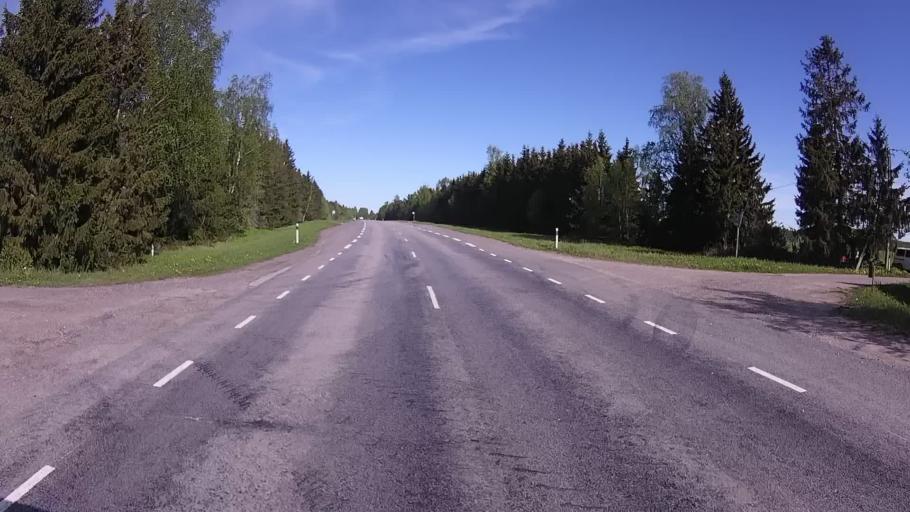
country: EE
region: Polvamaa
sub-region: Polva linn
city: Polva
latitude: 58.2413
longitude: 27.0117
